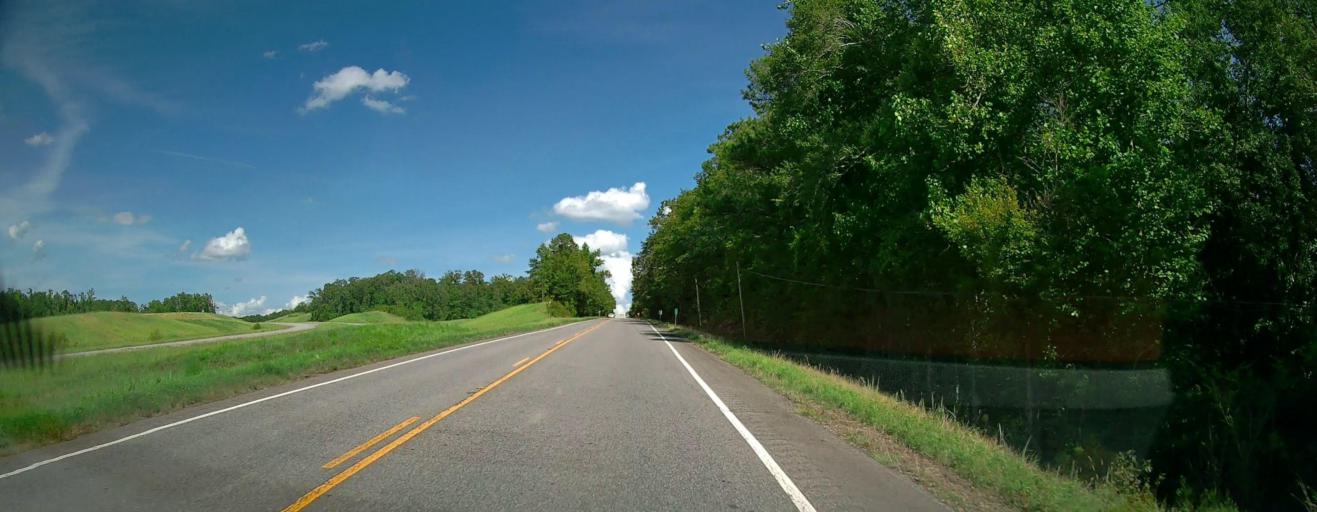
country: US
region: Alabama
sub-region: Pickens County
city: Gordo
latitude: 33.3341
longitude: -87.9239
